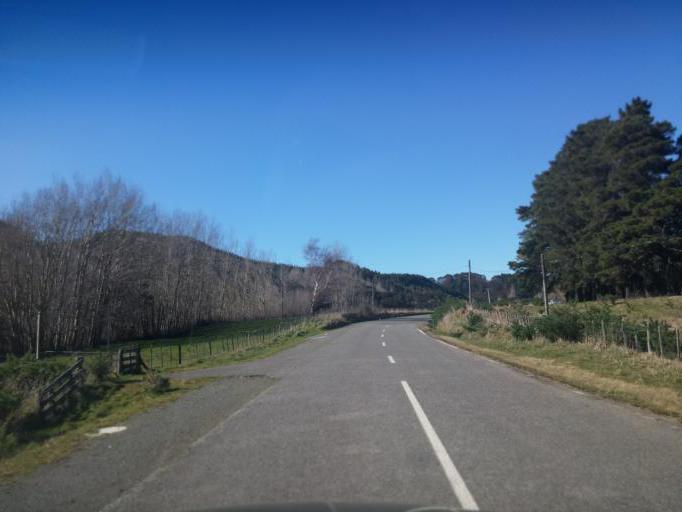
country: NZ
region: Wellington
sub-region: South Wairarapa District
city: Waipawa
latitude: -41.4310
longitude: 175.5103
